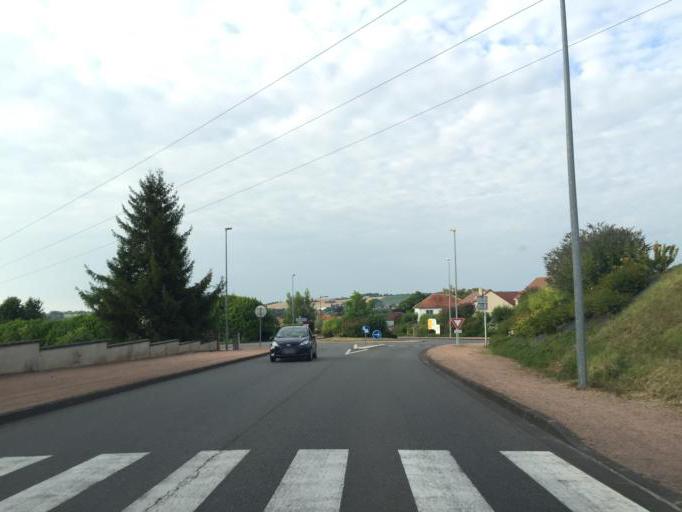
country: FR
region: Auvergne
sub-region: Departement de l'Allier
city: Saint-Germain-des-Fosses
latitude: 46.1940
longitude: 3.4319
